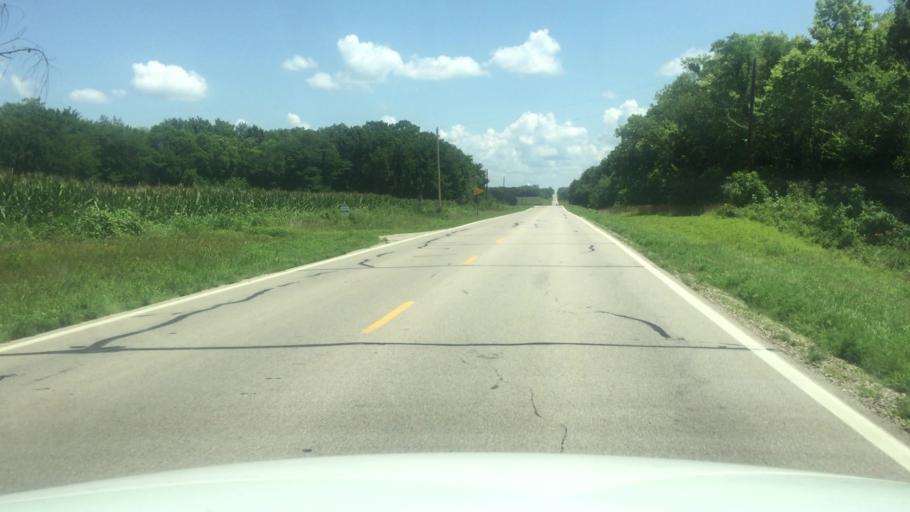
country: US
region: Kansas
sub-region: Brown County
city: Horton
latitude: 39.6674
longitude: -95.5574
